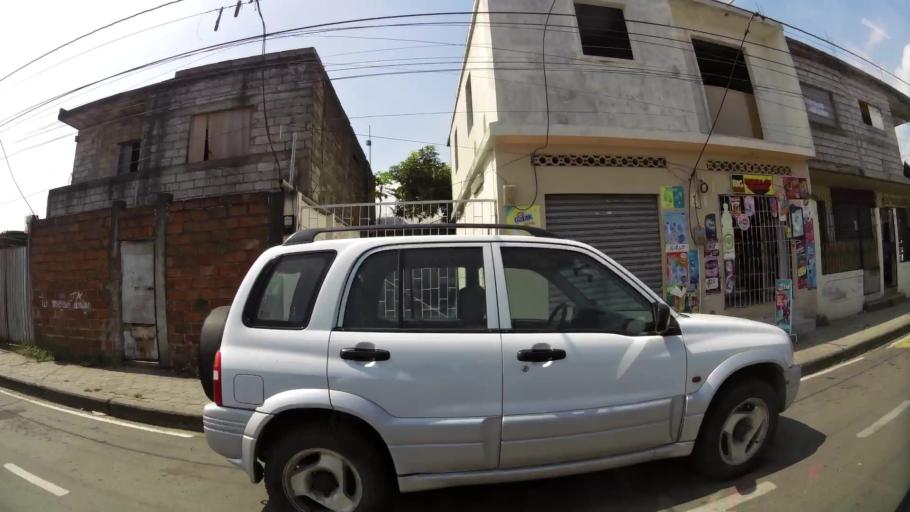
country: EC
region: Guayas
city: Eloy Alfaro
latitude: -2.1573
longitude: -79.8412
